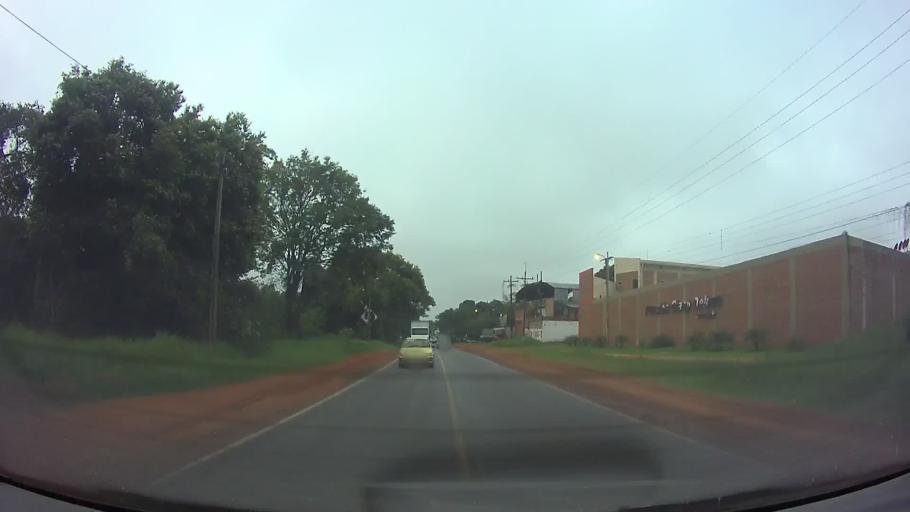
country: PY
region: Central
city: Itaugua
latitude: -25.4104
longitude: -57.3600
